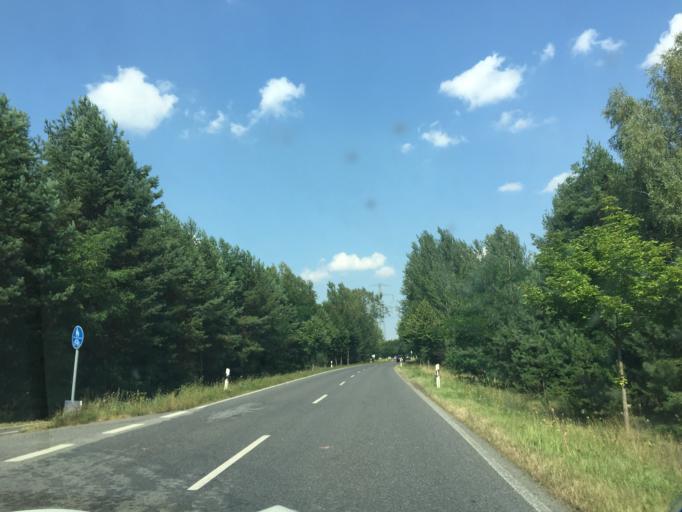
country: DE
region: Saxony
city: Boxberg
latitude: 51.4154
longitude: 14.5503
